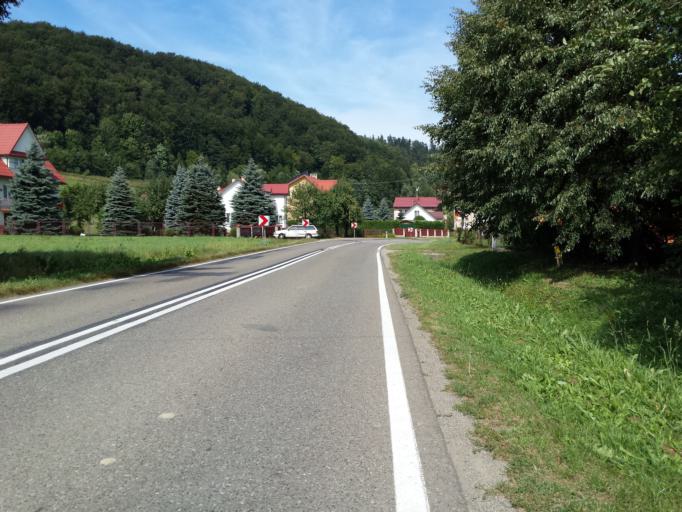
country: PL
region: Subcarpathian Voivodeship
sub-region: Powiat leski
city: Baligrod
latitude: 49.3936
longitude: 22.2815
